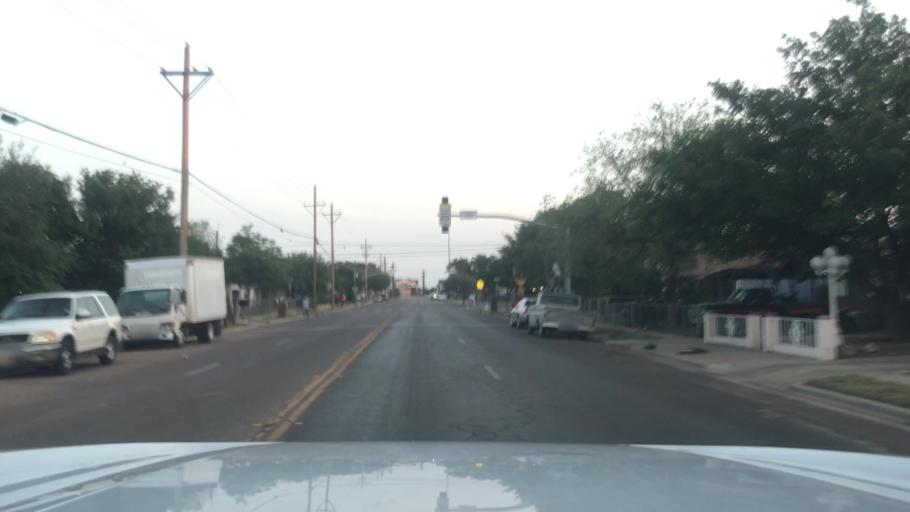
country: US
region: Texas
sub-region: Lubbock County
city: Lubbock
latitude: 33.5969
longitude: -101.8619
